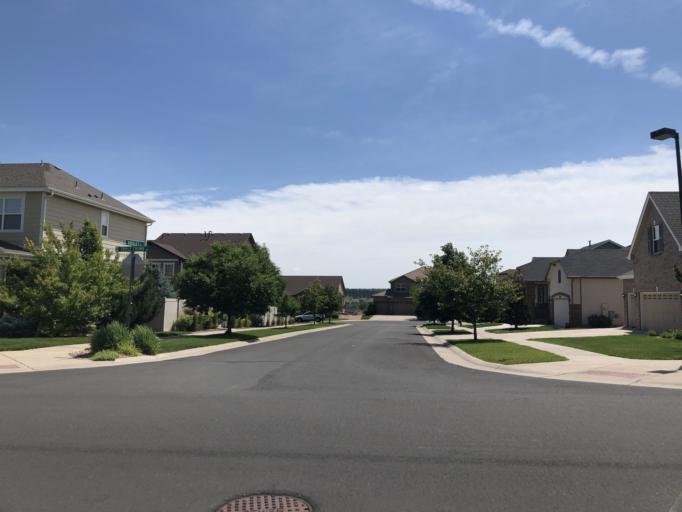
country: US
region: Colorado
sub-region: Douglas County
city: Parker
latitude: 39.4974
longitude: -104.7823
